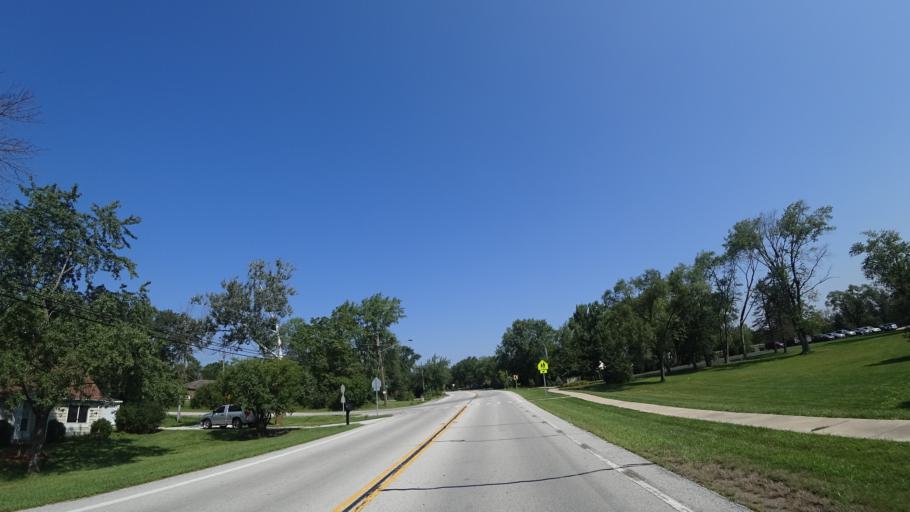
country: US
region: Illinois
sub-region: Cook County
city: Oak Forest
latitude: 41.5770
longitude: -87.7551
